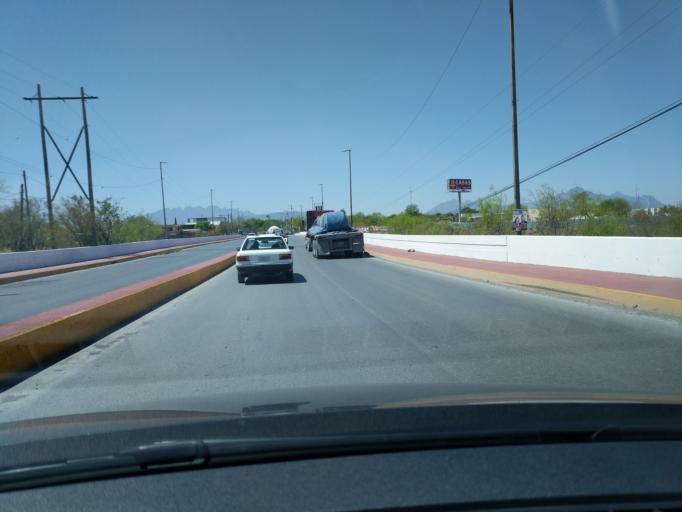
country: MX
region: Nuevo Leon
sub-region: Apodaca
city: Artemio Trevino
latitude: 25.8171
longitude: -100.1502
